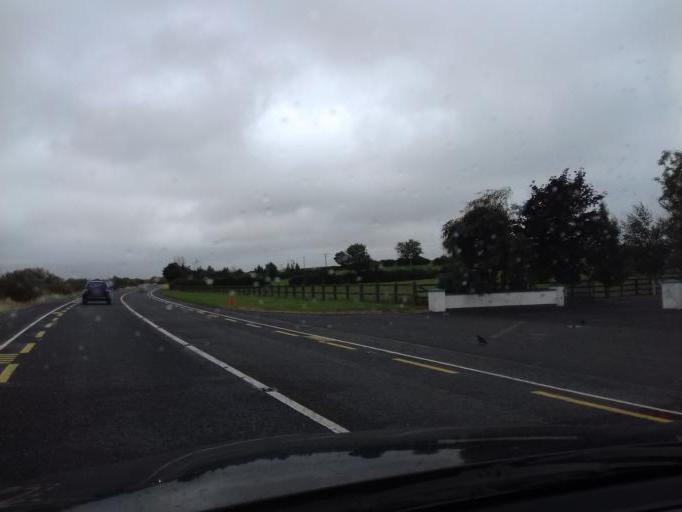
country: IE
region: Leinster
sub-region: County Carlow
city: Bagenalstown
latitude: 52.7481
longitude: -6.9667
